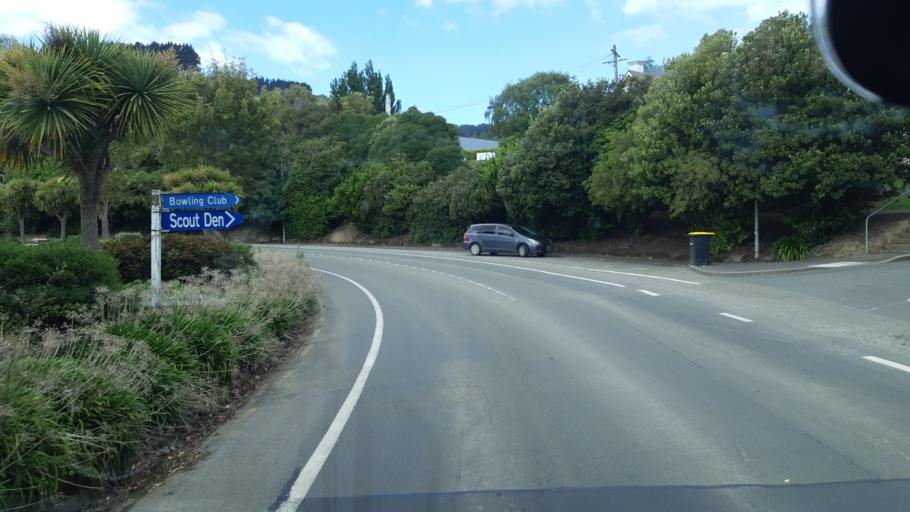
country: NZ
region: Otago
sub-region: Dunedin City
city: Portobello
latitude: -45.8696
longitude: 170.5963
